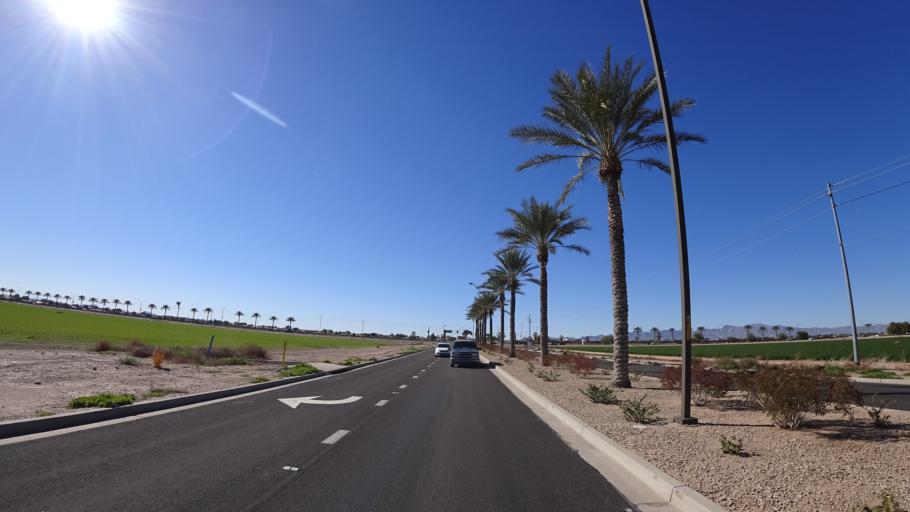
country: US
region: Arizona
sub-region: Maricopa County
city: Goodyear
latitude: 33.4354
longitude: -112.3903
